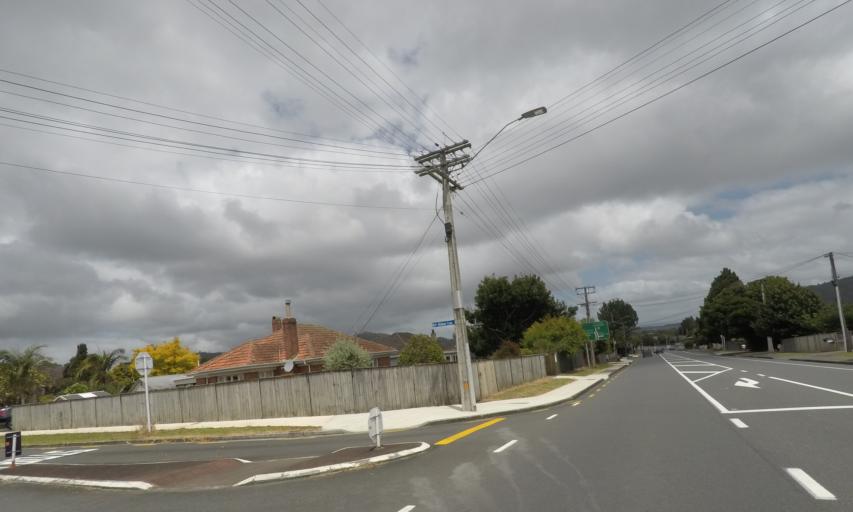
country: NZ
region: Northland
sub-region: Whangarei
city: Whangarei
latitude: -35.6963
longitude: 174.3120
